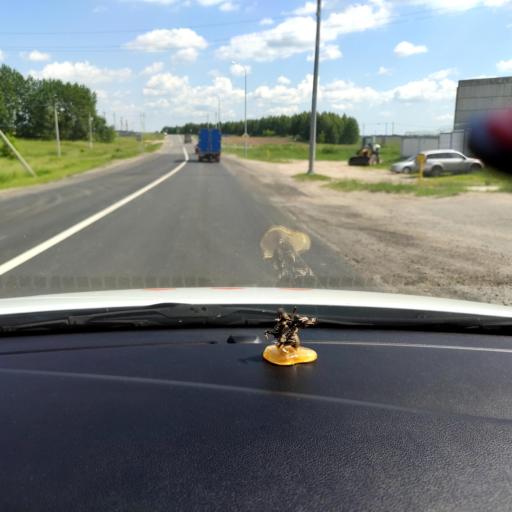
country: RU
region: Tatarstan
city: Stolbishchi
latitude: 55.6199
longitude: 49.1562
